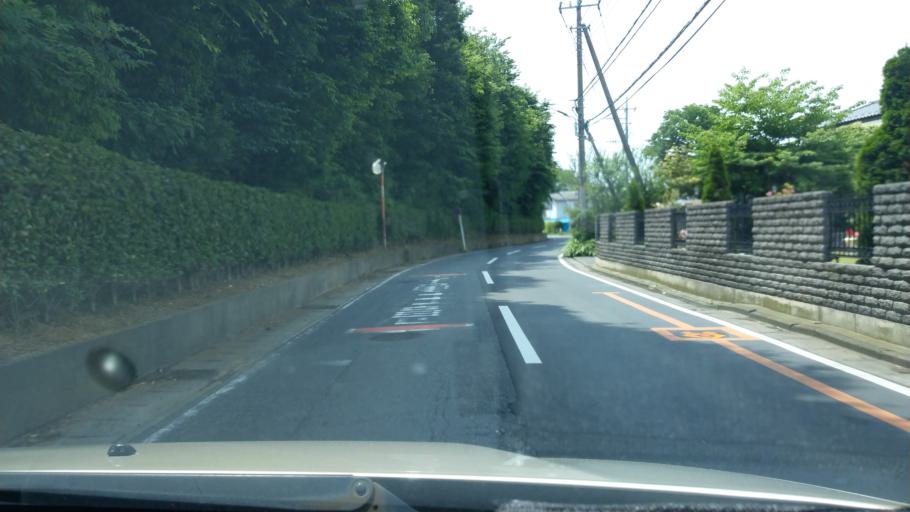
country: JP
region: Saitama
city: Saitama
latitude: 35.9076
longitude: 139.6504
